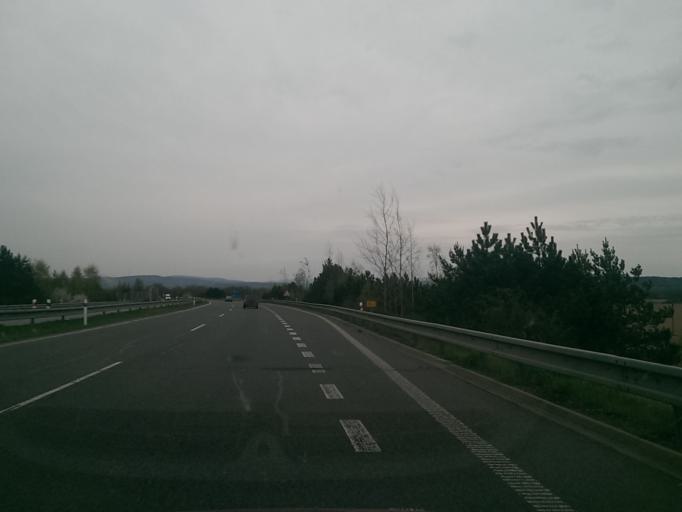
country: CZ
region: Central Bohemia
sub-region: Okres Mlada Boleslav
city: Zd'ar
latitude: 50.5431
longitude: 15.0384
